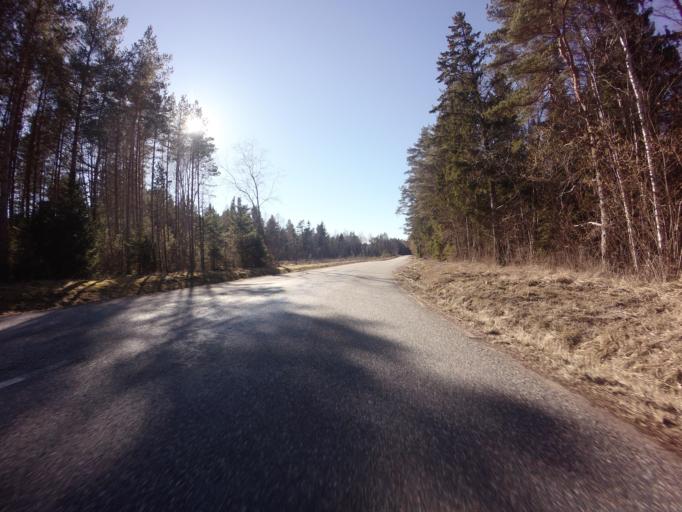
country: EE
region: Saare
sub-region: Kuressaare linn
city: Kuressaare
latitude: 58.5695
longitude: 22.4213
